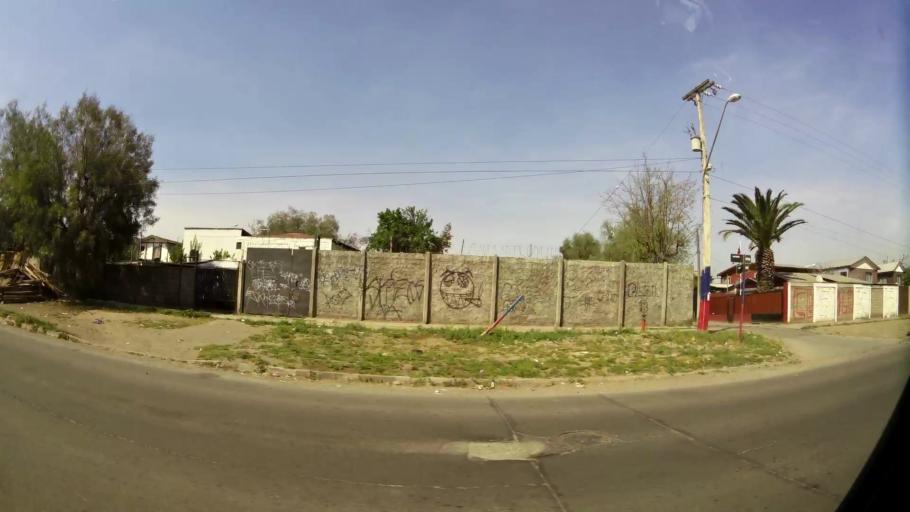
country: CL
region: Santiago Metropolitan
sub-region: Provincia de Santiago
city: Lo Prado
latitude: -33.4287
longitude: -70.7690
